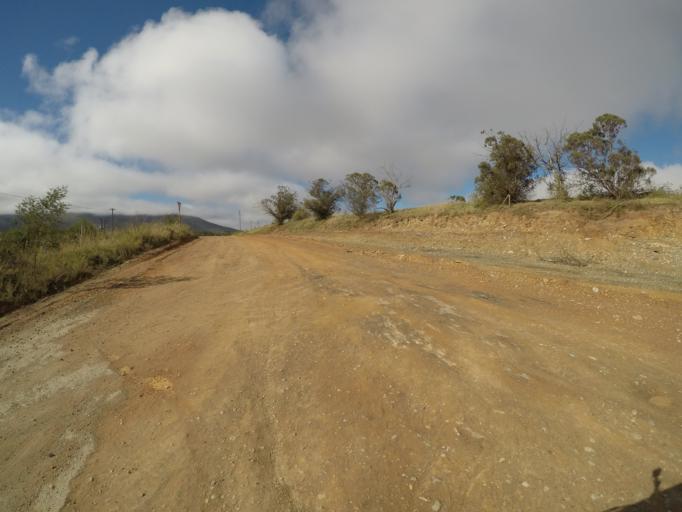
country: ZA
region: Western Cape
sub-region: Cape Winelands District Municipality
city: Ashton
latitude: -34.1284
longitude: 19.8405
